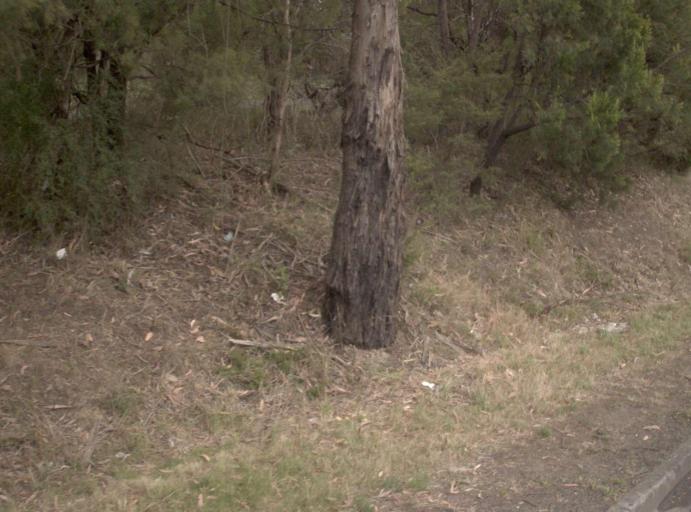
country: AU
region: Victoria
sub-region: Yarra Ranges
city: Launching Place
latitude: -37.7863
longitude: 145.5588
